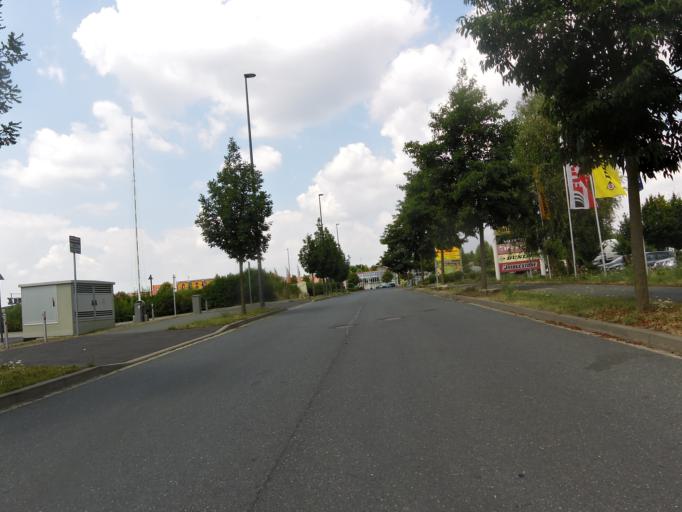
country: DE
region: Bavaria
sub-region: Regierungsbezirk Unterfranken
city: Randersacker
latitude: 49.7301
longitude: 9.9592
